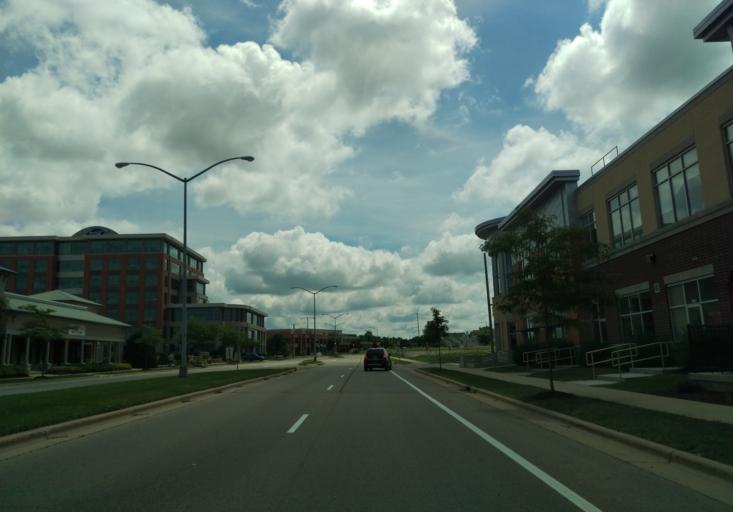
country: US
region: Wisconsin
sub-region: Dane County
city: Middleton
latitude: 43.0735
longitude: -89.5266
